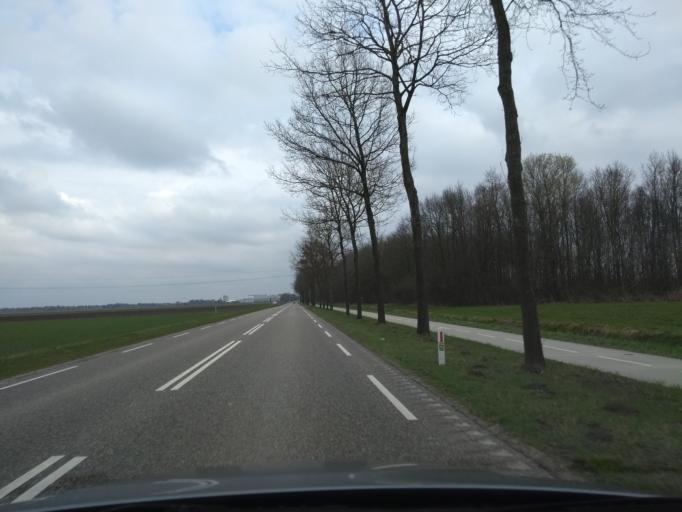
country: NL
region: Overijssel
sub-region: Gemeente Steenwijkerland
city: Vollenhove
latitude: 52.6900
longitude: 5.9316
